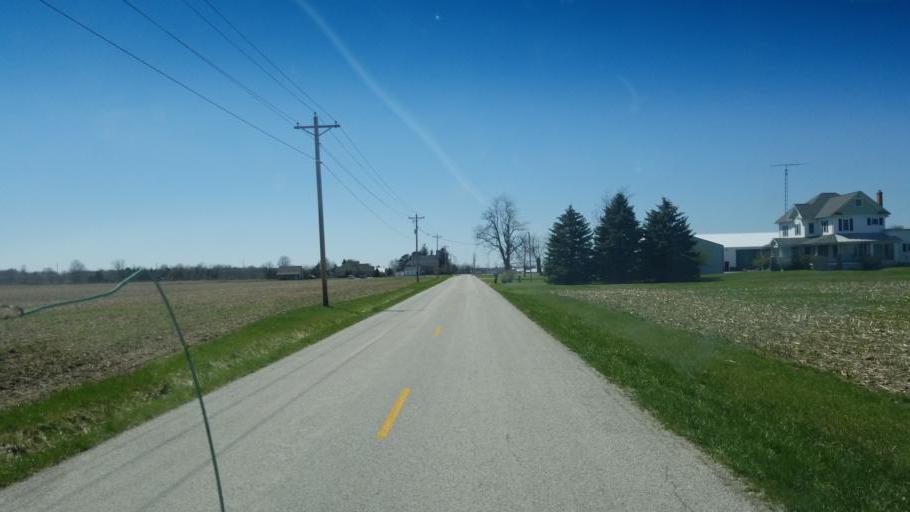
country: US
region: Ohio
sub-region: Crawford County
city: Bucyrus
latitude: 41.0229
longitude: -82.9498
